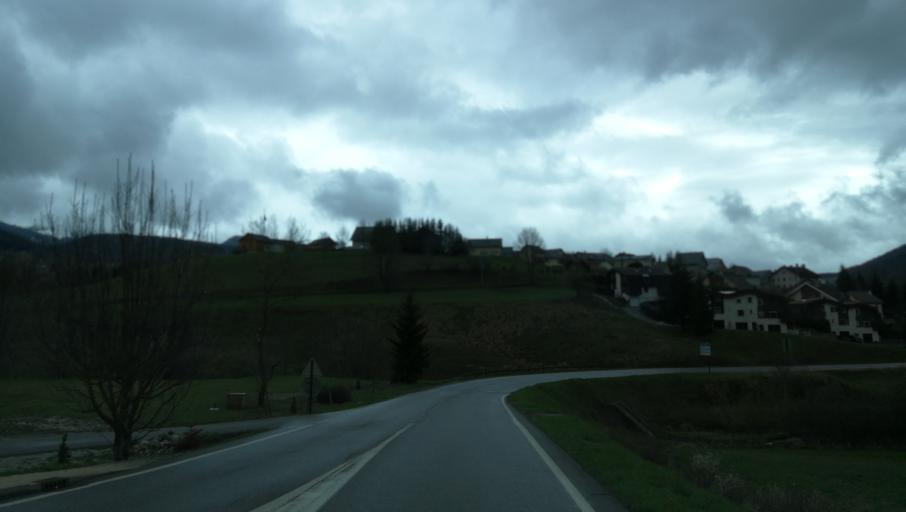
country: FR
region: Rhone-Alpes
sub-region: Departement de l'Isere
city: Villard-de-Lans
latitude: 45.0790
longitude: 5.5534
